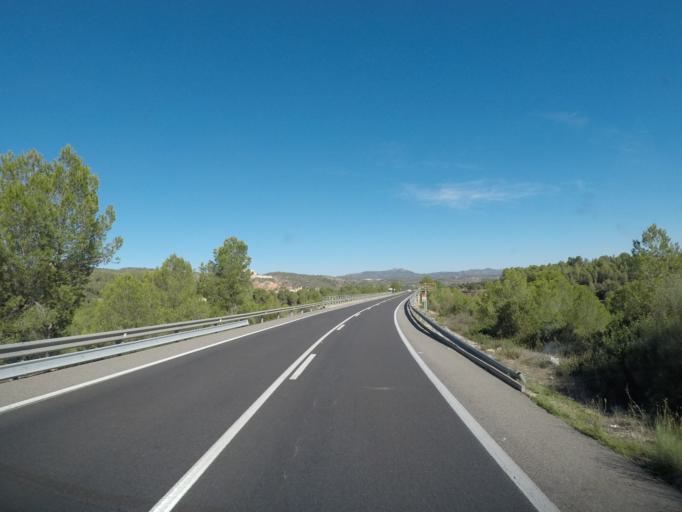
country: ES
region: Catalonia
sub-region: Provincia de Tarragona
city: Miravet
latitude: 41.0237
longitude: 0.6048
